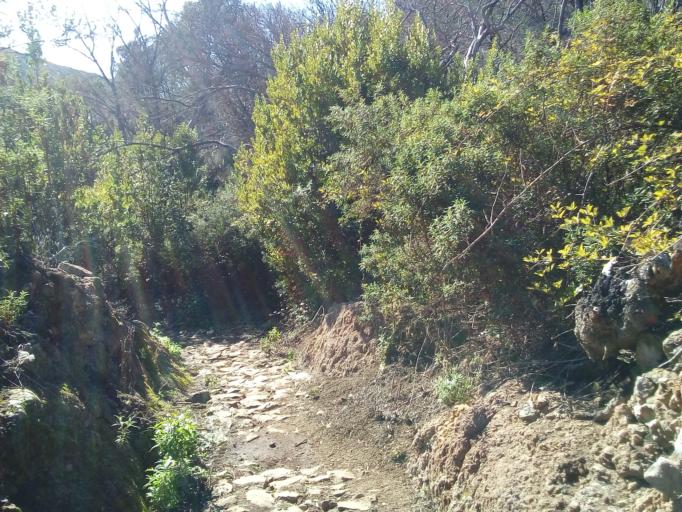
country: ES
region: Canary Islands
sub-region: Provincia de Santa Cruz de Tenerife
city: Vallehermosa
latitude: 28.1228
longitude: -17.2642
